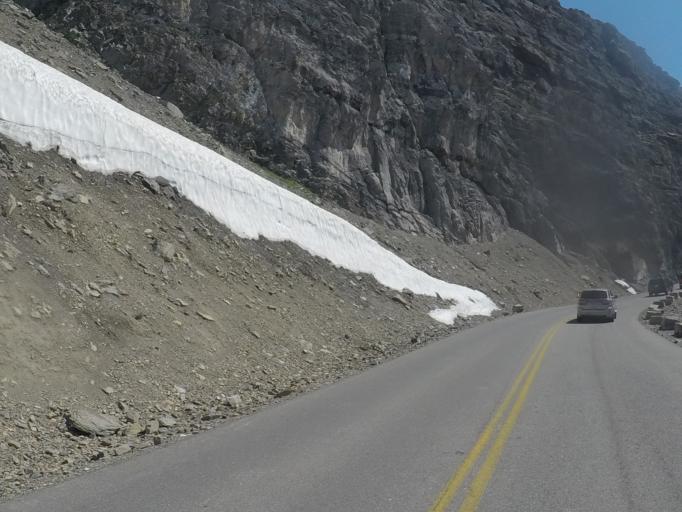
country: US
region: Montana
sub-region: Flathead County
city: Columbia Falls
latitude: 48.7014
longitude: -113.7179
